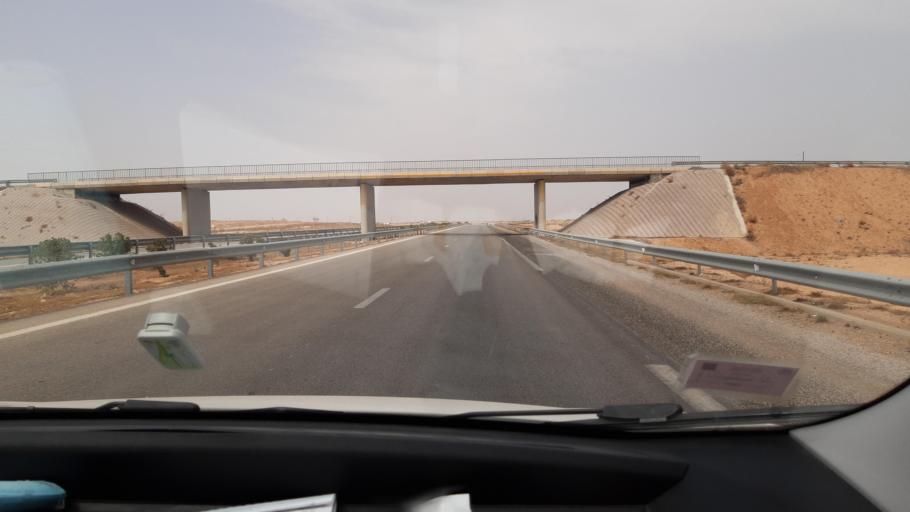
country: TN
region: Safaqis
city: Sfax
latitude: 34.7676
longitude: 10.6097
